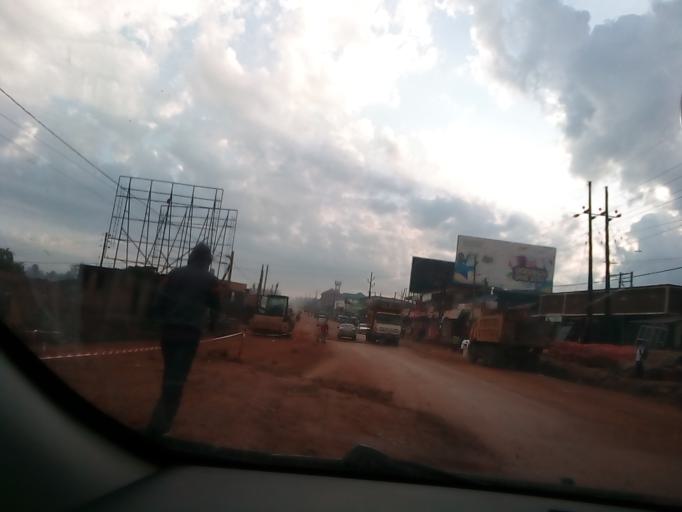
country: UG
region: Central Region
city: Masaka
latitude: -0.3187
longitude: 31.7589
